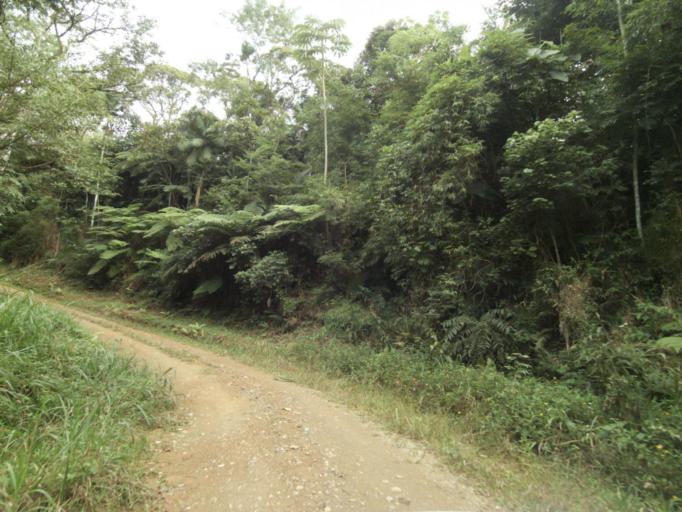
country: BR
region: Santa Catarina
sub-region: Pomerode
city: Pomerode
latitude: -26.7403
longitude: -49.1874
